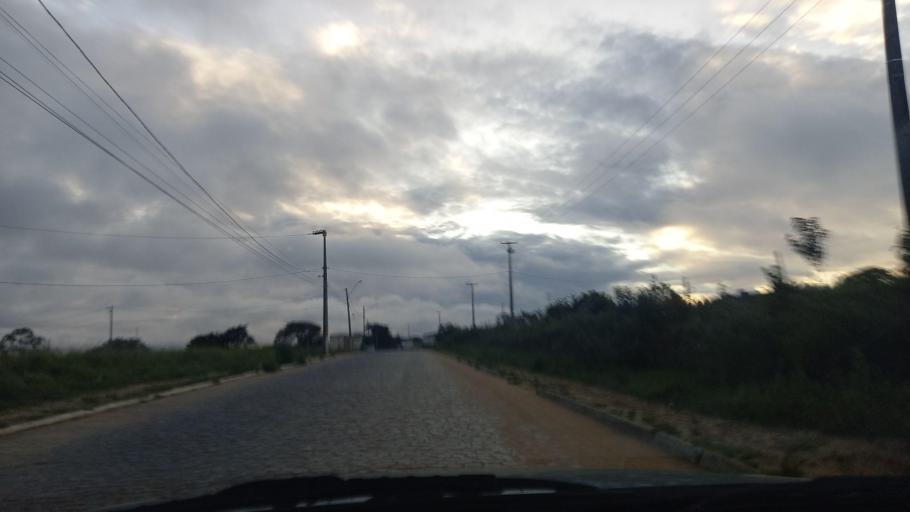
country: BR
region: Pernambuco
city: Garanhuns
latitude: -8.8908
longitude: -36.4470
